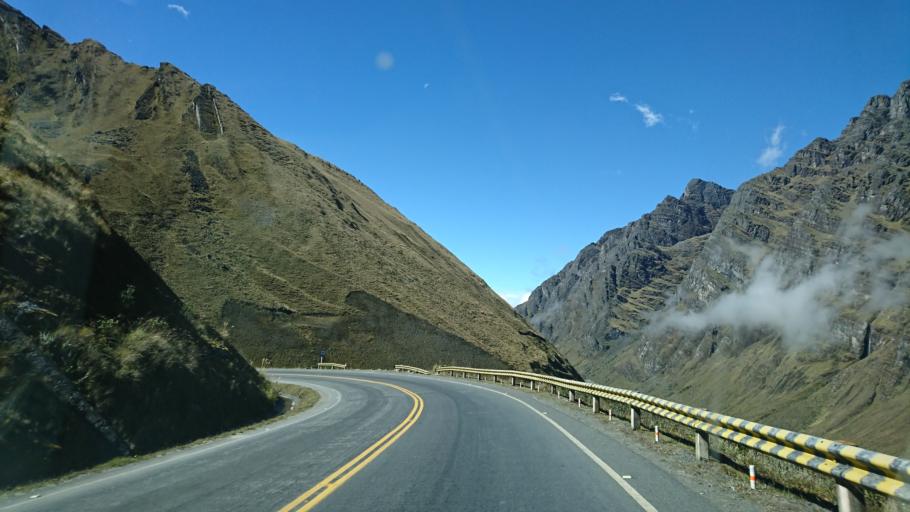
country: BO
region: La Paz
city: La Paz
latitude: -16.3292
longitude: -67.9574
